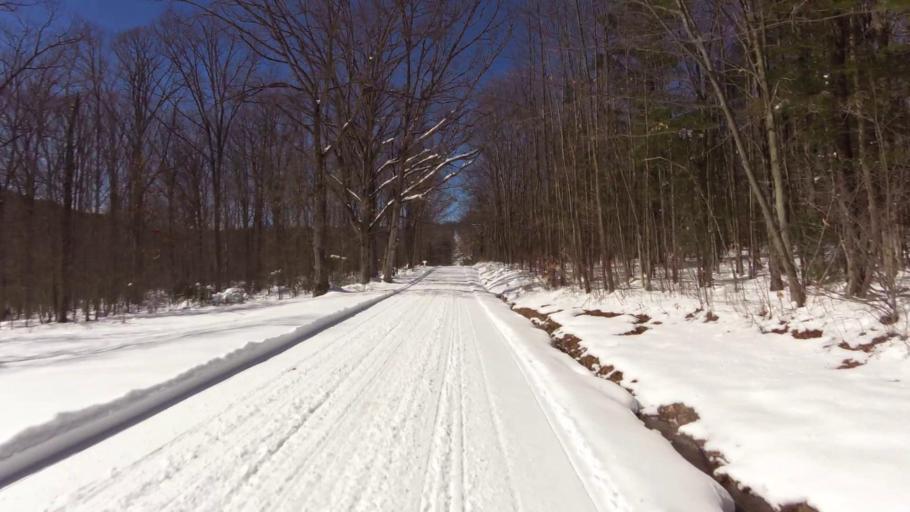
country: US
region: New York
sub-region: Allegany County
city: Houghton
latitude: 42.3267
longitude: -78.2175
